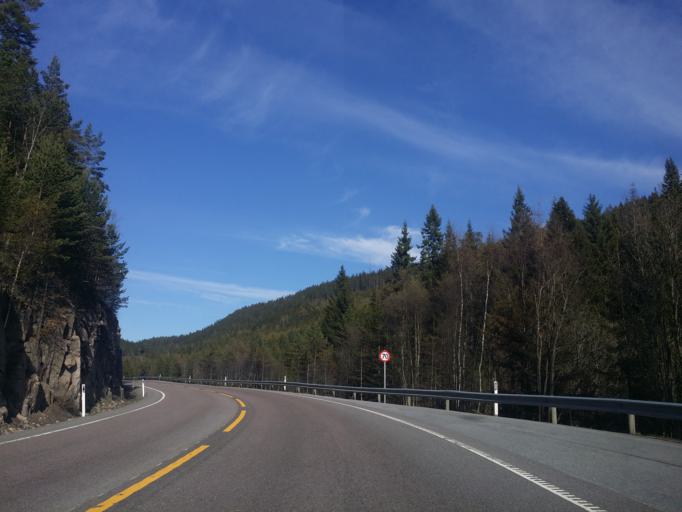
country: NO
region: Telemark
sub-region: Notodden
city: Notodden
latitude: 59.5986
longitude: 9.3989
